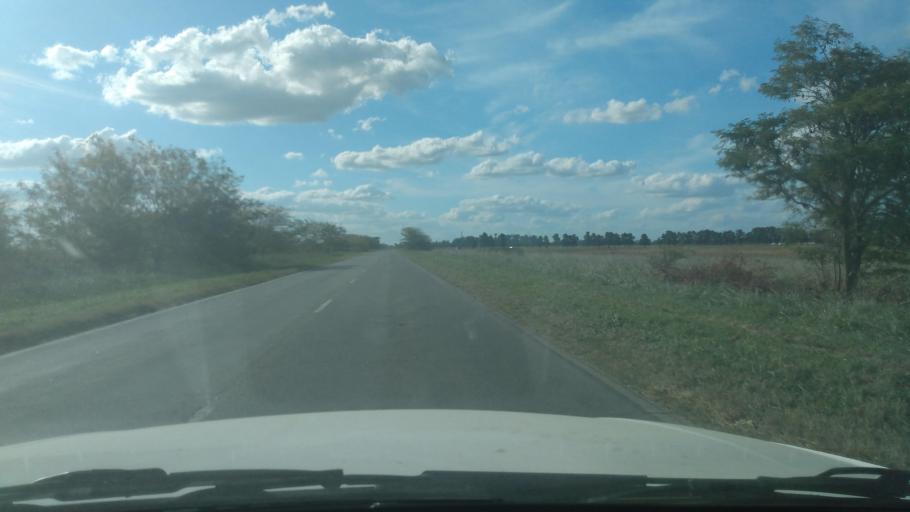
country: AR
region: Buenos Aires
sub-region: Partido de Navarro
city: Navarro
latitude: -34.9744
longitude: -59.3170
